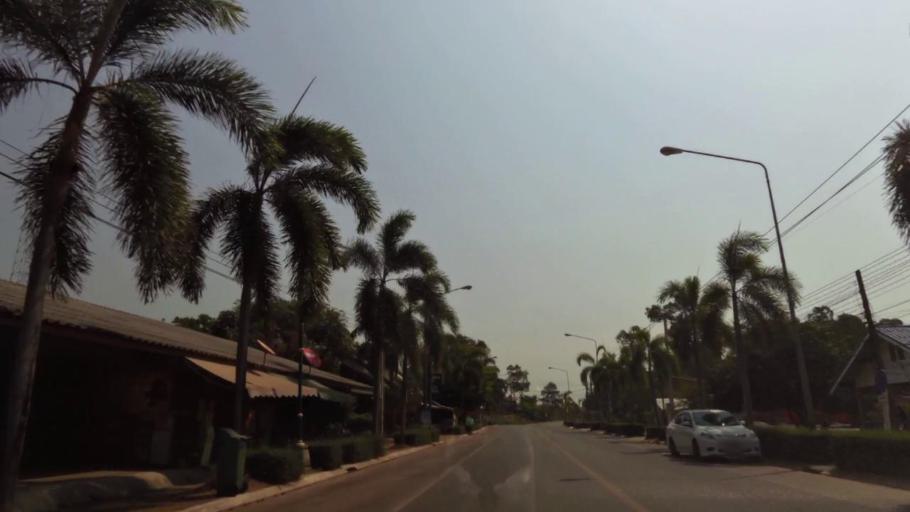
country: TH
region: Chanthaburi
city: Tha Mai
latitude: 12.5509
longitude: 101.9248
